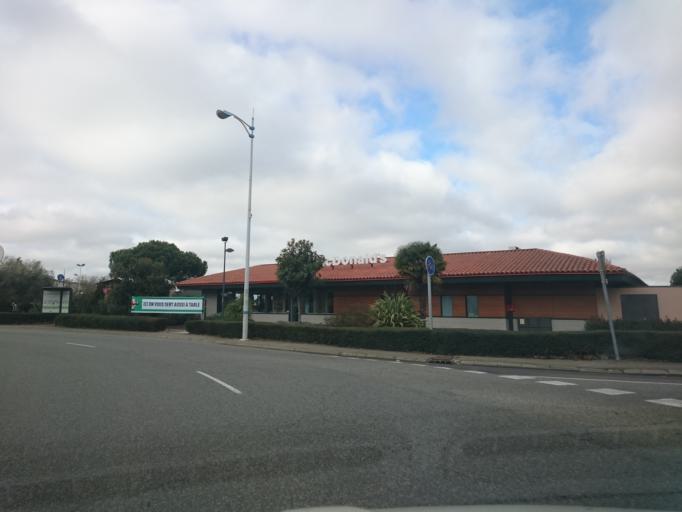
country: FR
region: Midi-Pyrenees
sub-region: Departement de la Haute-Garonne
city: Colomiers
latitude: 43.6133
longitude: 1.3311
